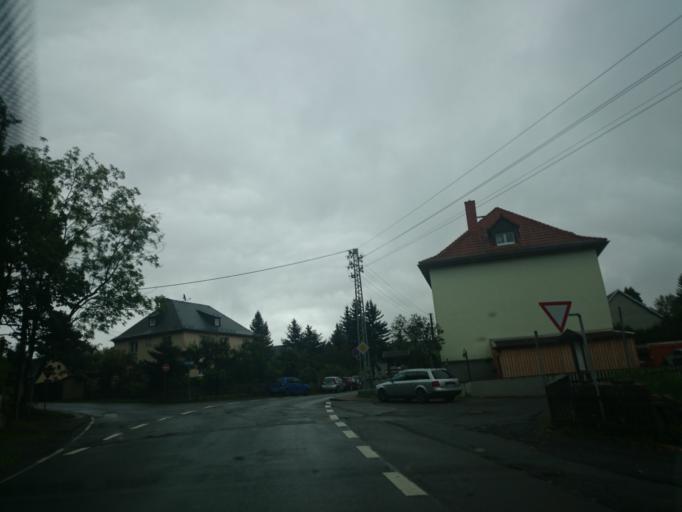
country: DE
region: Saxony
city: Brand-Erbisdorf
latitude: 50.8676
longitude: 13.3186
